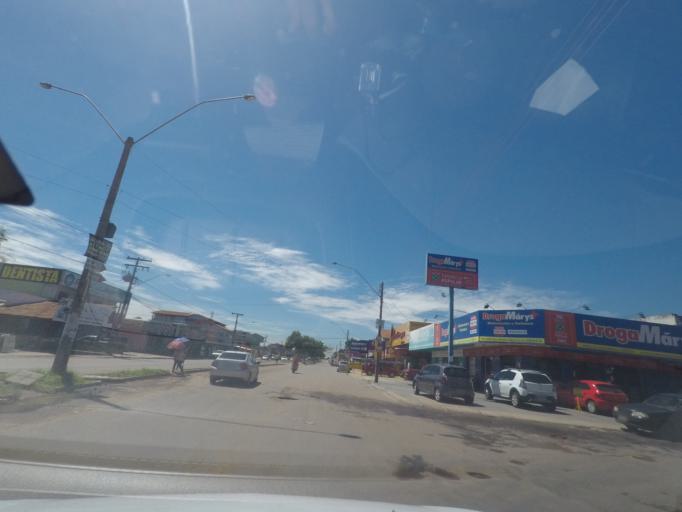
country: BR
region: Goias
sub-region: Aparecida De Goiania
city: Aparecida de Goiania
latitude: -16.7653
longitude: -49.3485
